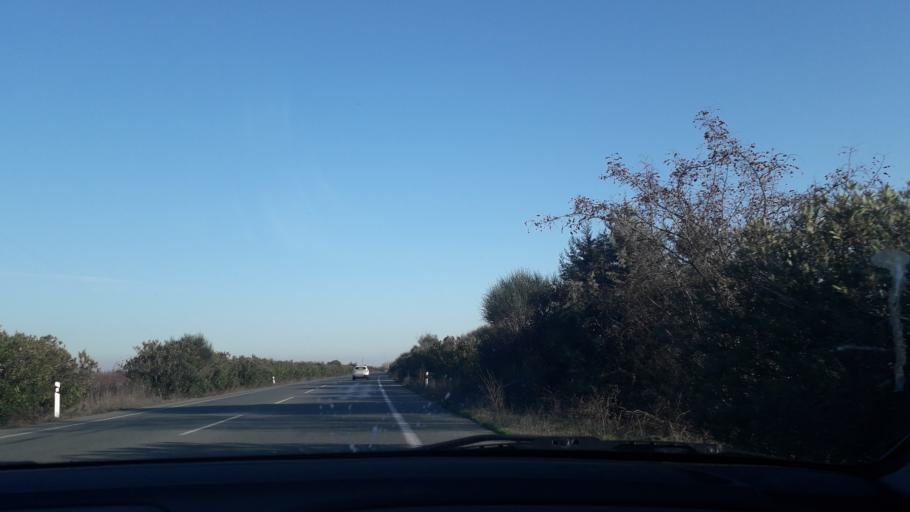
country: GR
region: Central Macedonia
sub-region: Nomos Pellis
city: Palaifyto
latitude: 40.8086
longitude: 22.2352
